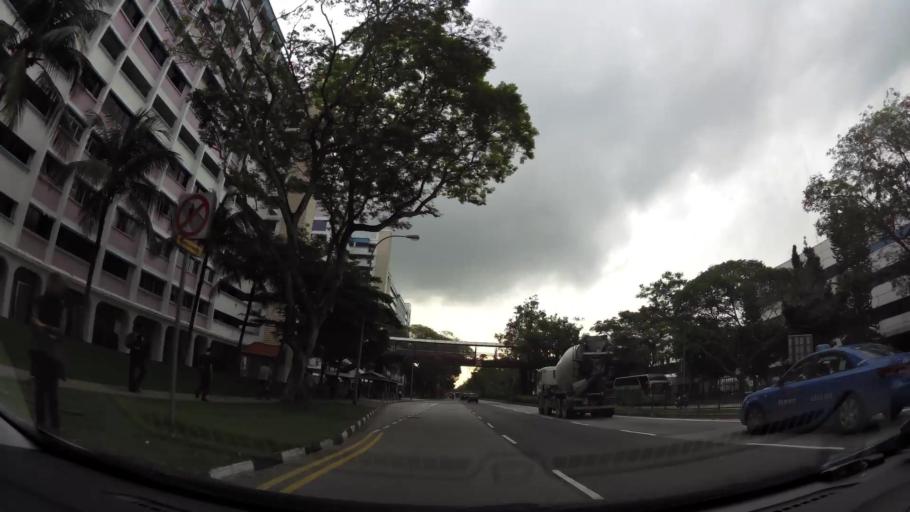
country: MY
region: Johor
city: Kampung Pasir Gudang Baru
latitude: 1.4406
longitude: 103.8385
